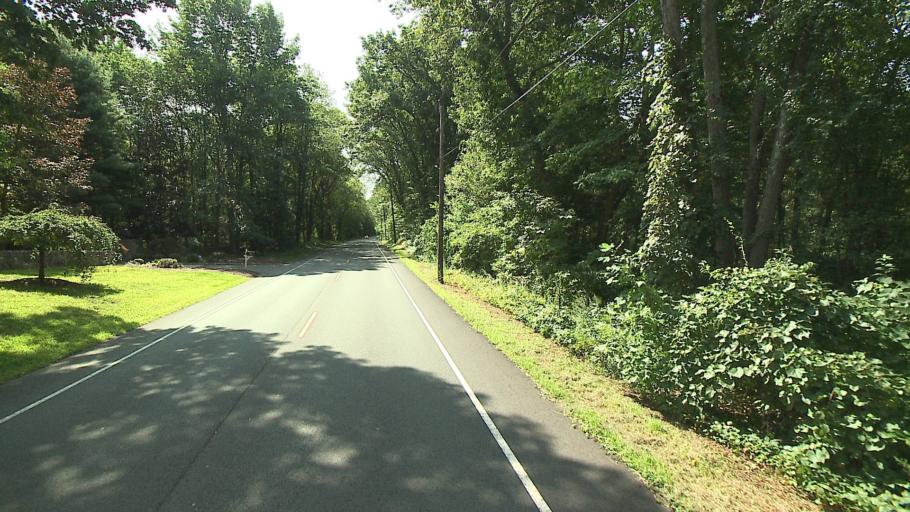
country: US
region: Connecticut
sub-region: Fairfield County
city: Trumbull
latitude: 41.2813
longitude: -73.2948
